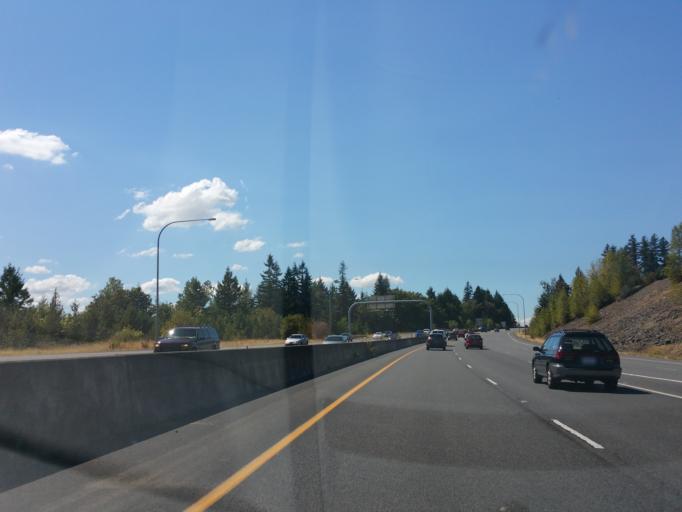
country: US
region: Washington
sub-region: Clark County
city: Mill Plain
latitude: 45.5853
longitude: -122.4767
